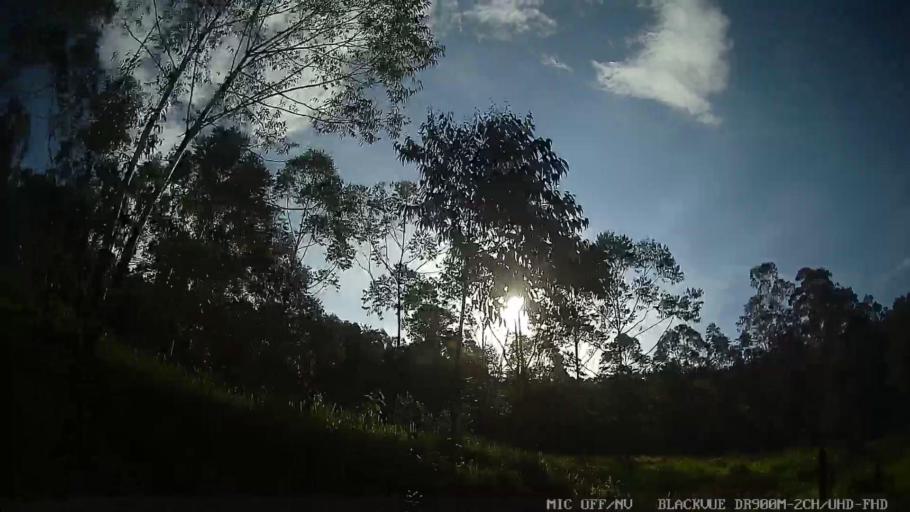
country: BR
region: Sao Paulo
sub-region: Serra Negra
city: Serra Negra
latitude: -22.6623
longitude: -46.6895
